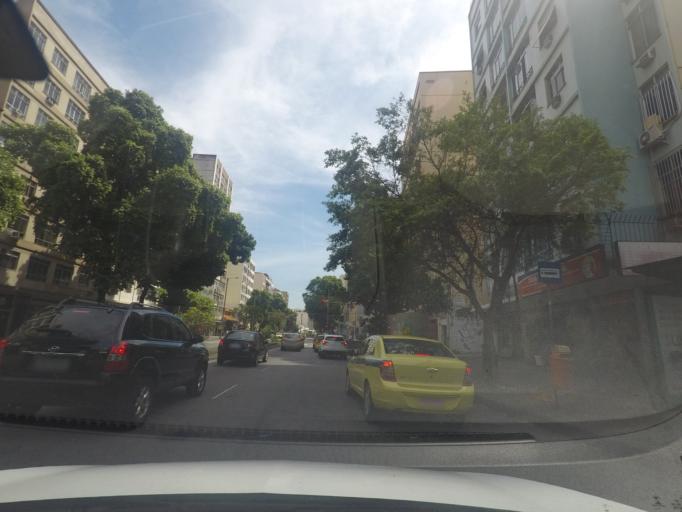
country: BR
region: Rio de Janeiro
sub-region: Rio De Janeiro
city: Rio de Janeiro
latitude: -22.9284
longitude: -43.2365
